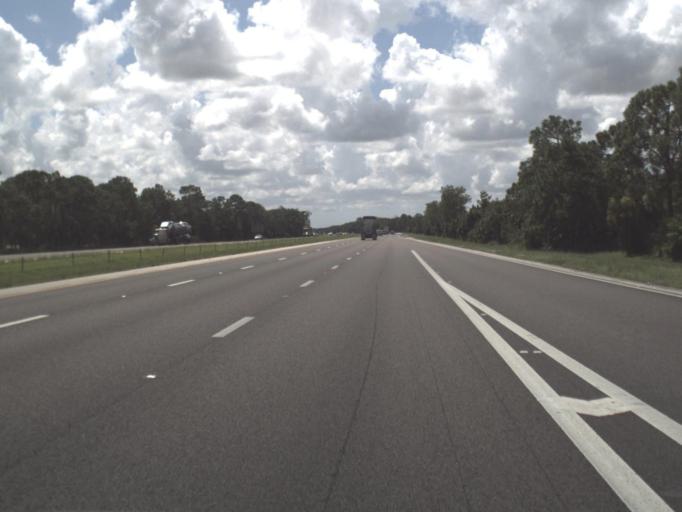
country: US
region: Florida
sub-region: Lee County
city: Bonita Springs
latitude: 26.3266
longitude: -81.7492
